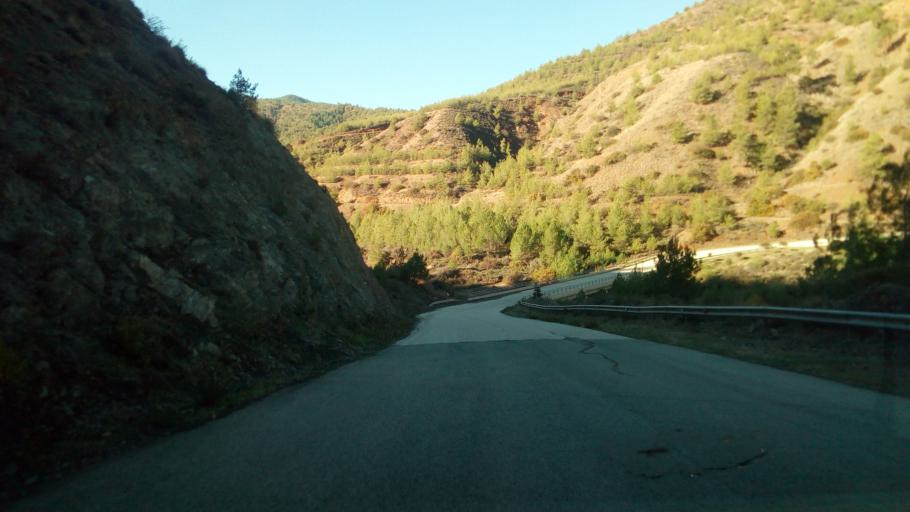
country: CY
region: Lefkosia
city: Lefka
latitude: 35.0734
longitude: 32.8046
